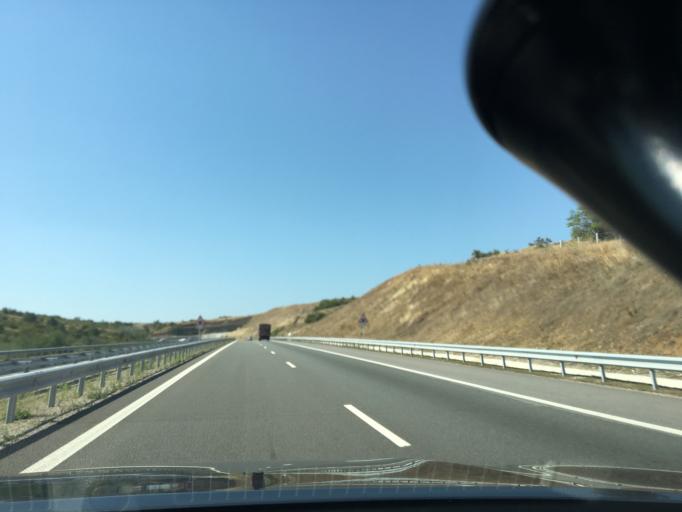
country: BG
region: Kyustendil
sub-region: Obshtina Dupnitsa
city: Dupnitsa
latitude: 42.2938
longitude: 23.0895
